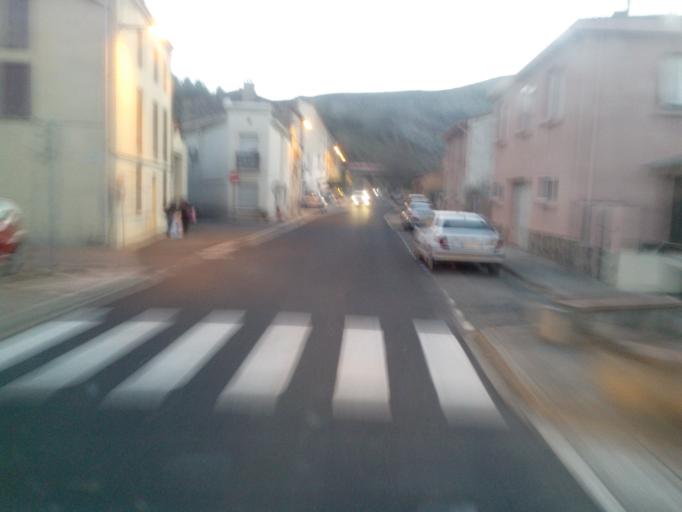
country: FR
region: Languedoc-Roussillon
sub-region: Departement des Pyrenees-Orientales
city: Baixas
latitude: 42.7779
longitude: 2.7893
